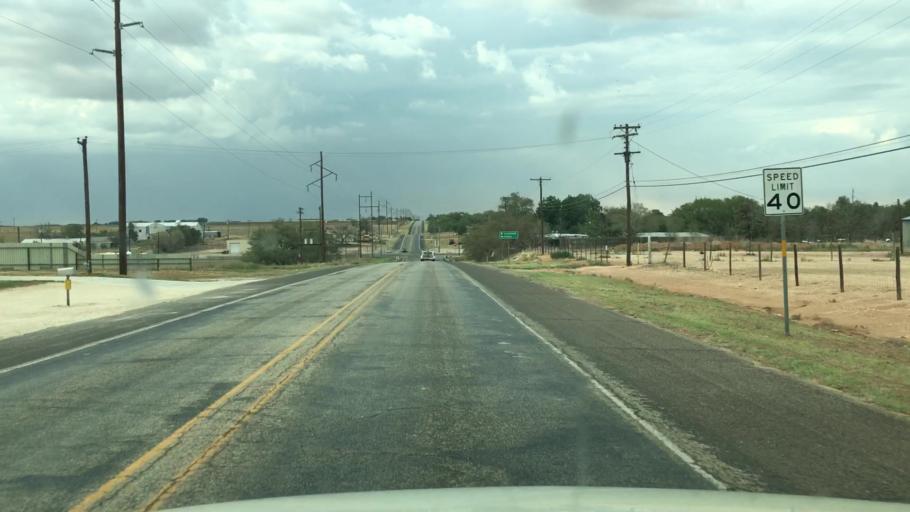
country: US
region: Texas
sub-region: Terry County
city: Brownfield
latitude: 33.1764
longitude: -102.2915
